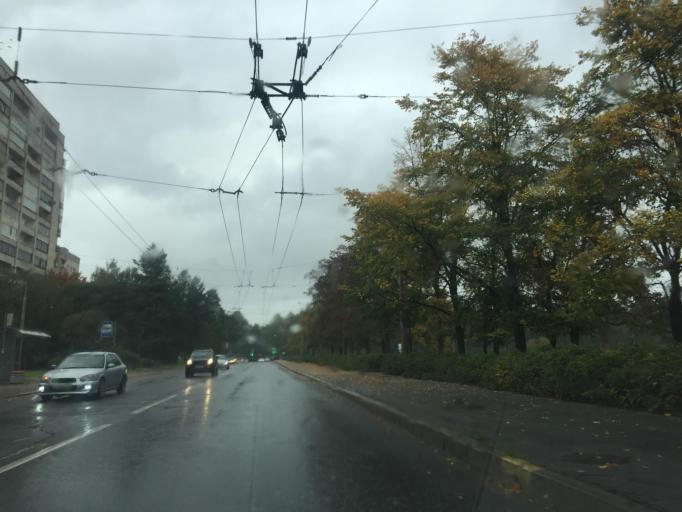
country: RU
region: St.-Petersburg
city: Sosnovka
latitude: 60.0116
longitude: 30.3565
